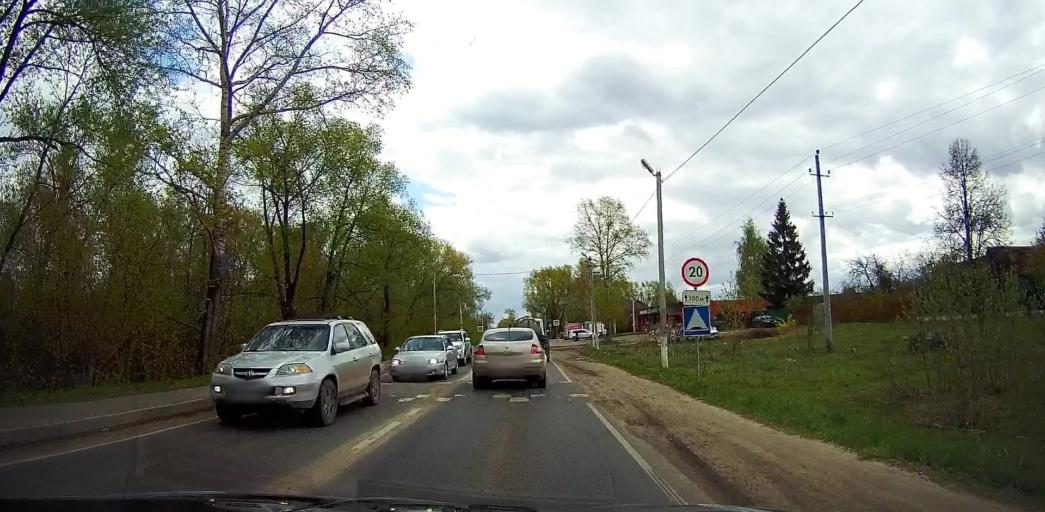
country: RU
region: Moskovskaya
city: Beloozerskiy
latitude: 55.4452
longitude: 38.4938
